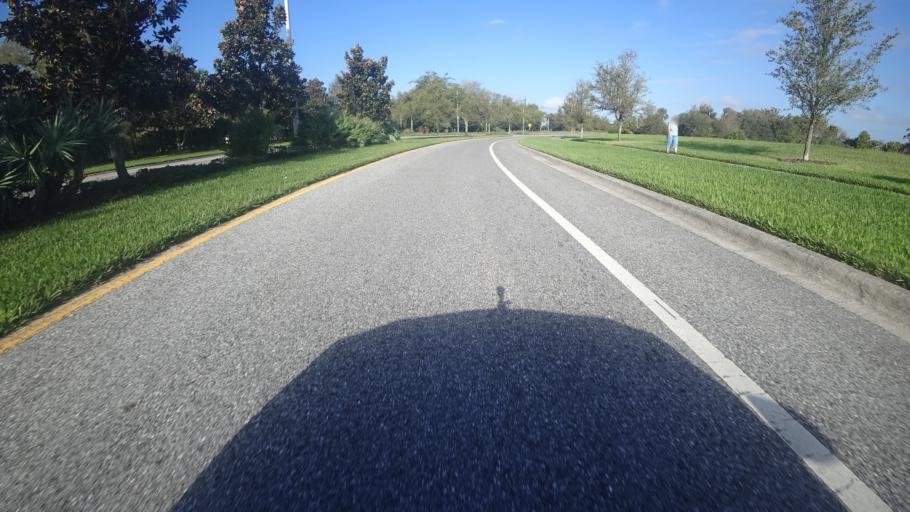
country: US
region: Florida
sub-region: Manatee County
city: Ellenton
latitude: 27.5577
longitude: -82.4567
